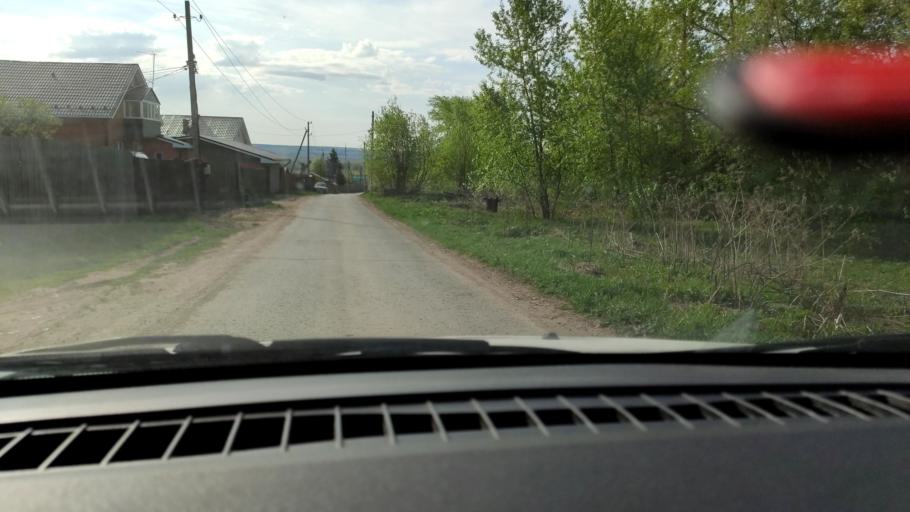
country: RU
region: Perm
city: Froly
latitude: 57.9469
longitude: 56.2989
